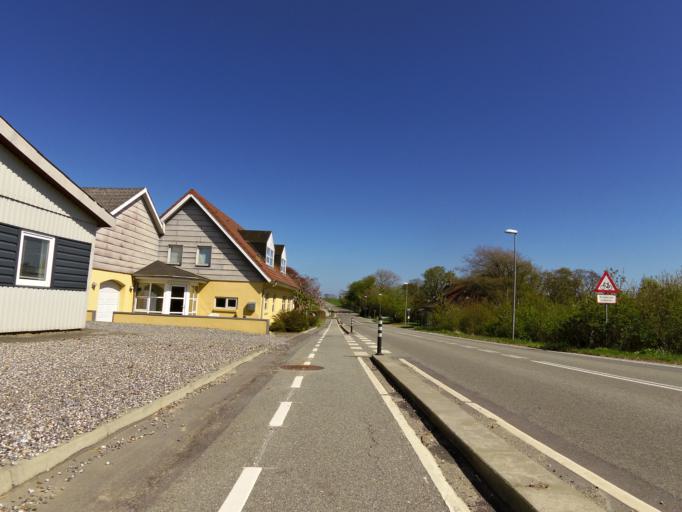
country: DK
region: Central Jutland
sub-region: Holstebro Kommune
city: Vinderup
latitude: 56.6001
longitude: 8.7576
